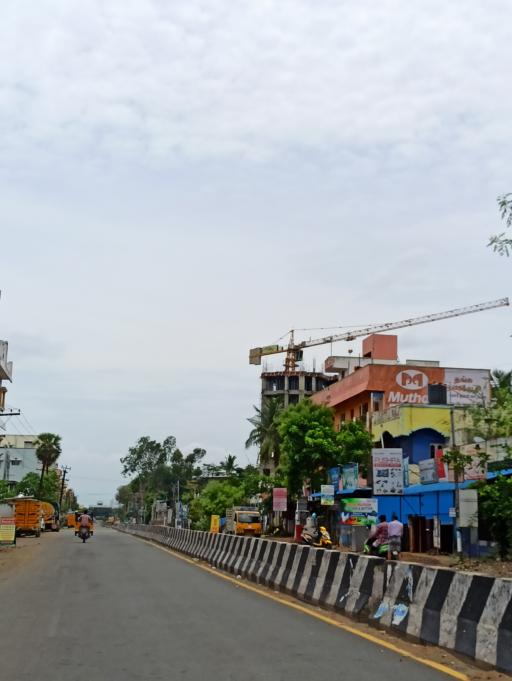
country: IN
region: Tamil Nadu
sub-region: Kancheepuram
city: Vandalur
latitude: 12.8960
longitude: 80.0646
